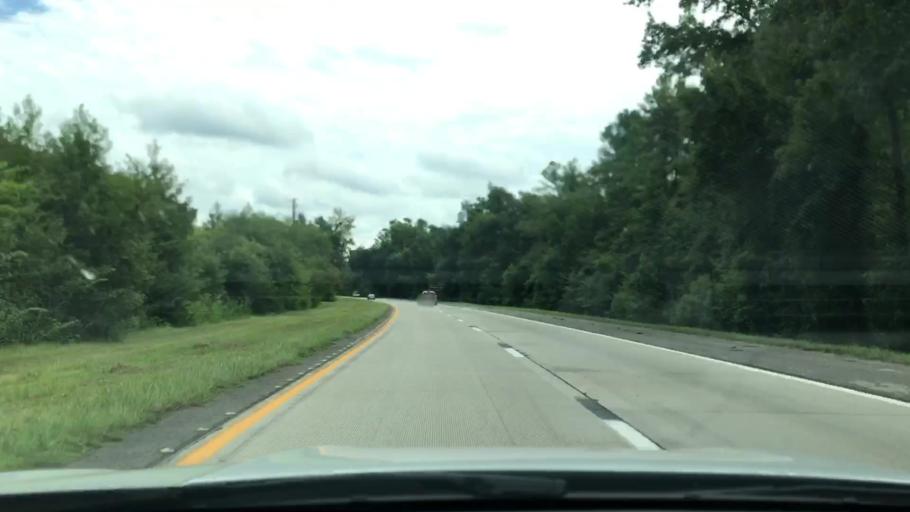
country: US
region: South Carolina
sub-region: Orangeburg County
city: Holly Hill
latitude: 33.2361
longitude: -80.4557
